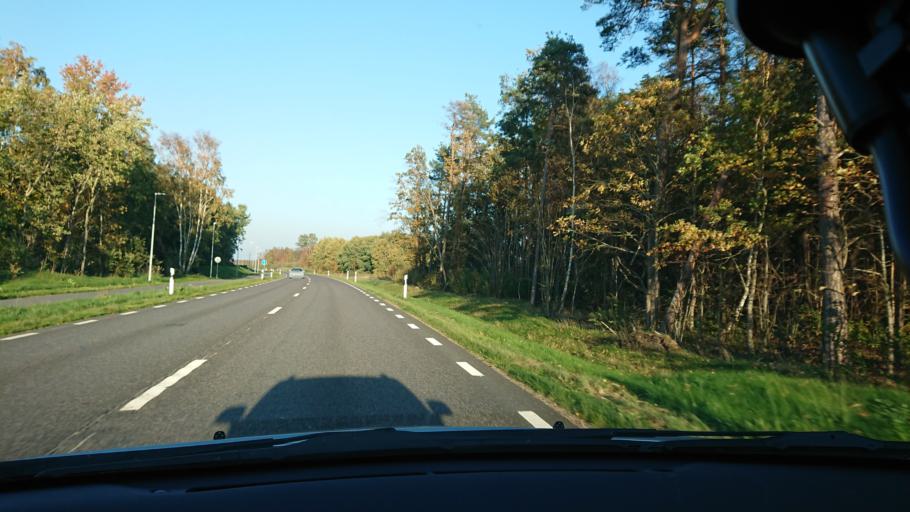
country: SE
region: Skane
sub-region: Bastads Kommun
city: Bastad
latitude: 56.4353
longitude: 12.9132
